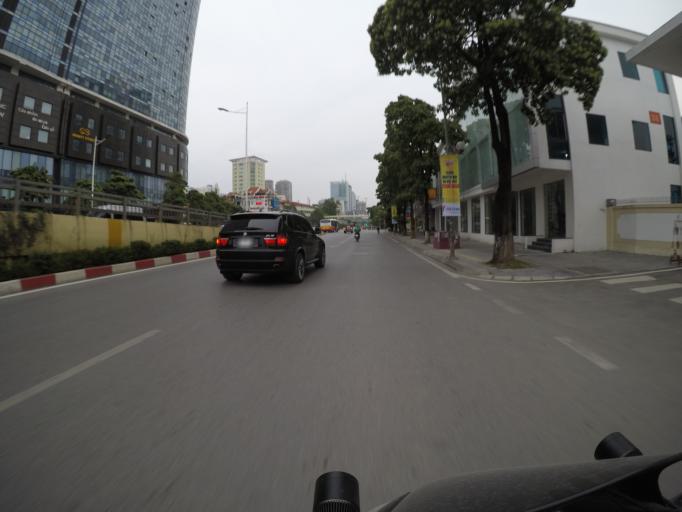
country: VN
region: Ha Noi
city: Cau Giay
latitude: 21.0143
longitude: 105.8034
